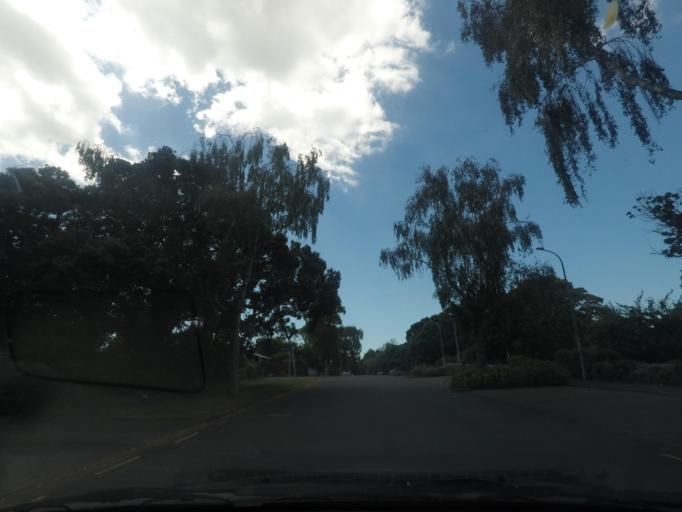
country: NZ
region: Auckland
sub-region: Auckland
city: Auckland
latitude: -36.8869
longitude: 174.7674
